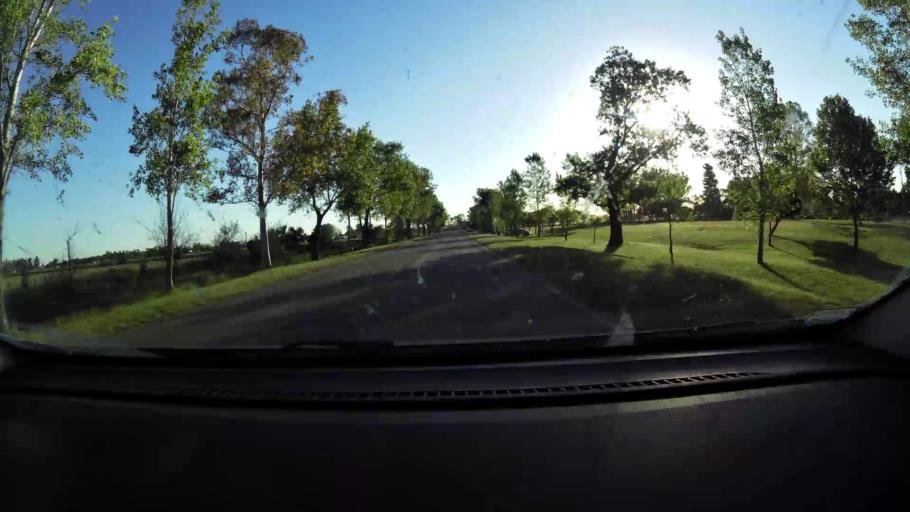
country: AR
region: Cordoba
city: Las Varillas
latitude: -31.8632
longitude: -62.7046
